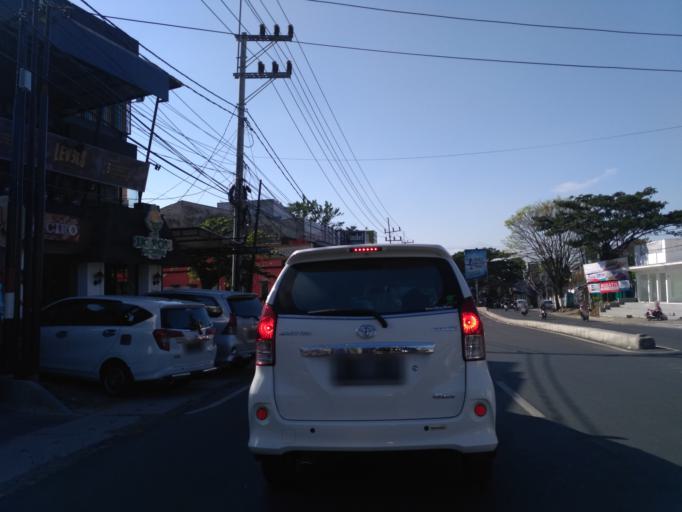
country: ID
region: East Java
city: Malang
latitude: -7.9392
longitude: 112.6362
